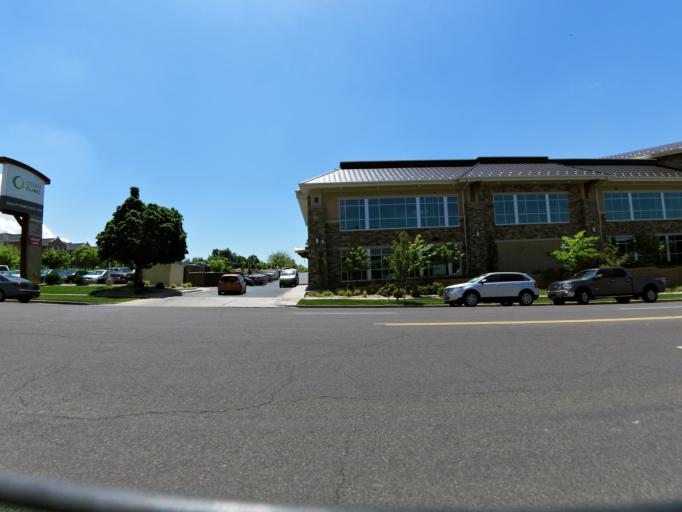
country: US
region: Utah
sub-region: Weber County
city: South Ogden
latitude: 41.1797
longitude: -111.9483
